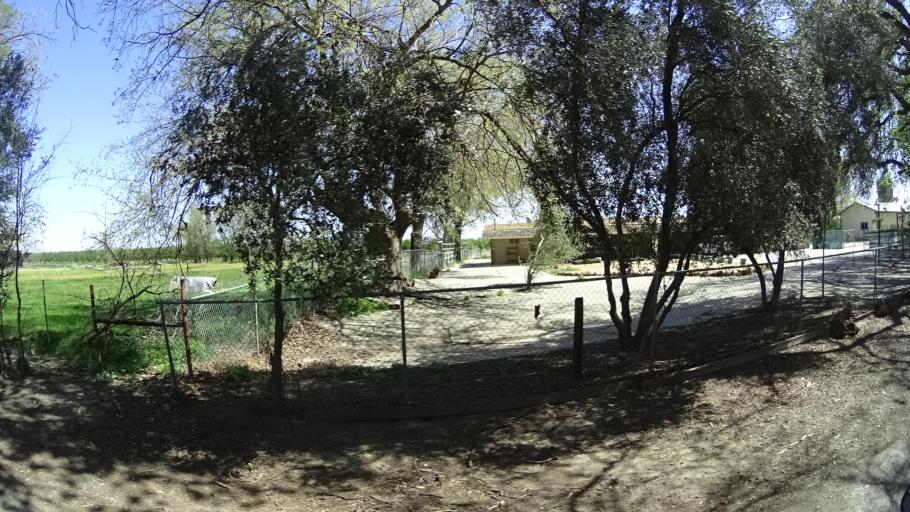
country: US
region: California
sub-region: Glenn County
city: Orland
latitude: 39.7844
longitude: -122.2721
